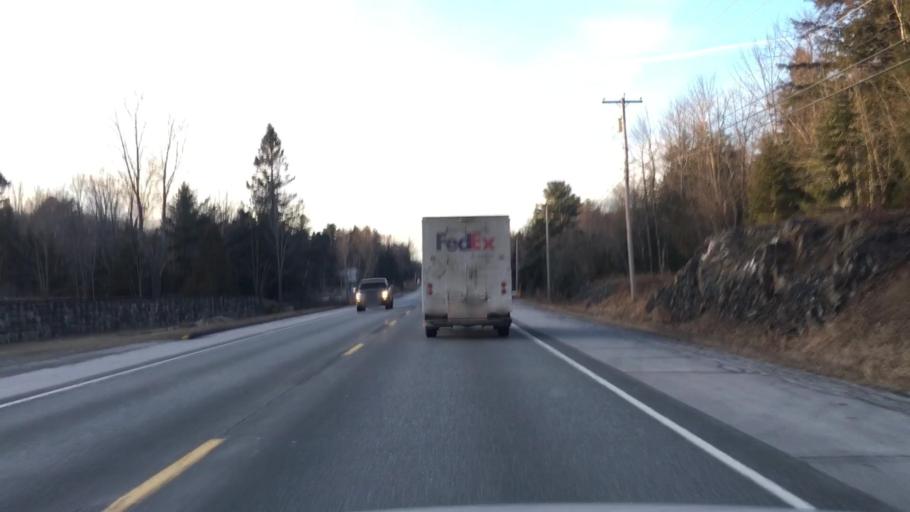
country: US
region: Maine
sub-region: Penobscot County
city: Holden
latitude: 44.7424
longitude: -68.6358
